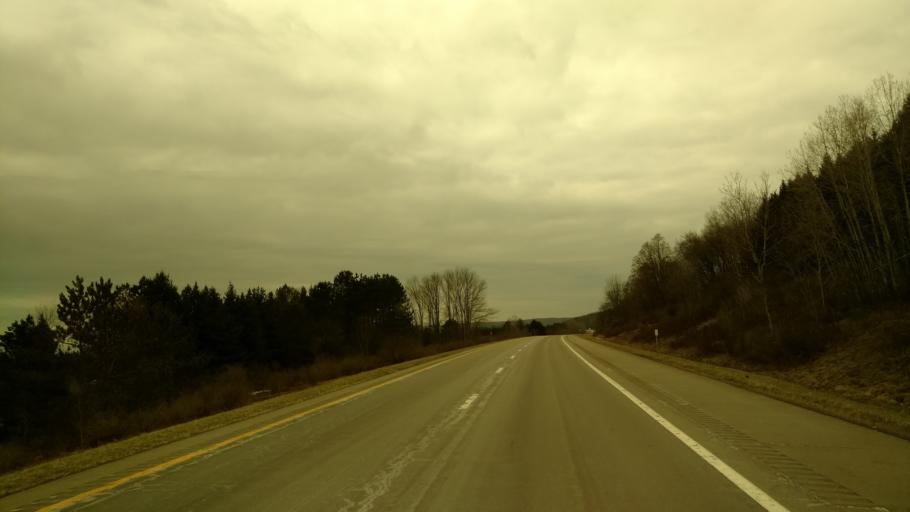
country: US
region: New York
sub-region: Chautauqua County
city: Falconer
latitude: 42.1352
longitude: -79.1439
